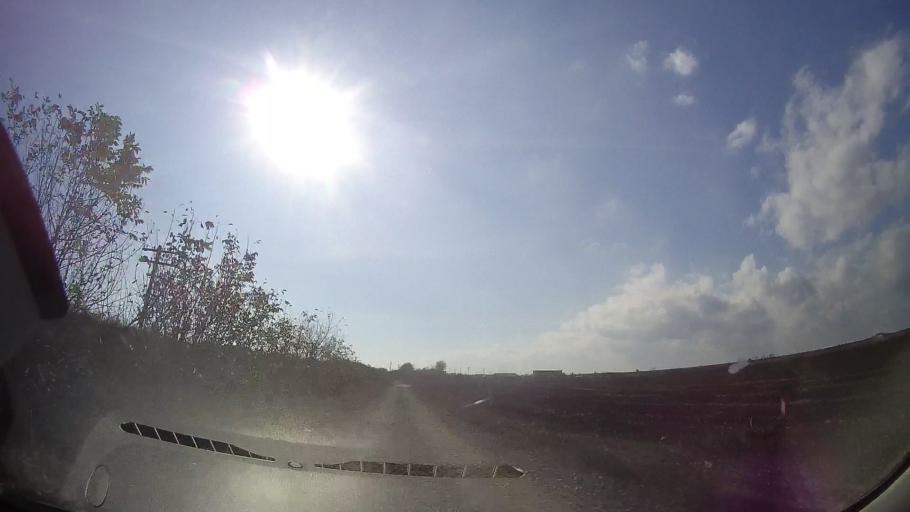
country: RO
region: Constanta
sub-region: Comuna Costinesti
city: Costinesti
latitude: 43.9656
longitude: 28.6398
